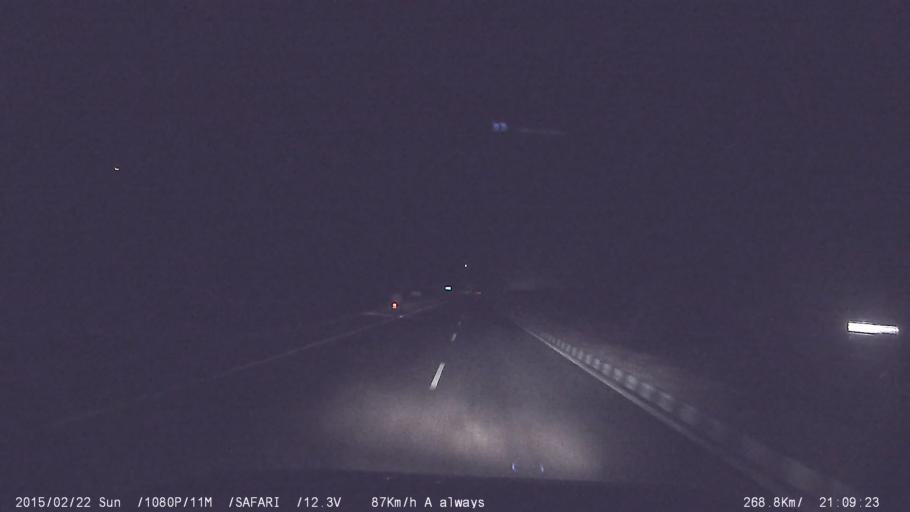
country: IN
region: Tamil Nadu
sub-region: Karur
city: Pallappatti
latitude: 10.7460
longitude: 77.9177
